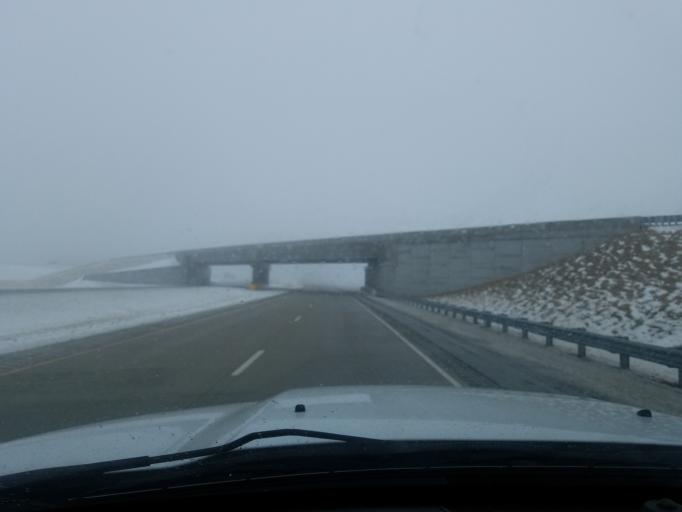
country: US
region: Indiana
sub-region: Howard County
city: Kokomo
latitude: 40.5344
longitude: -86.1119
